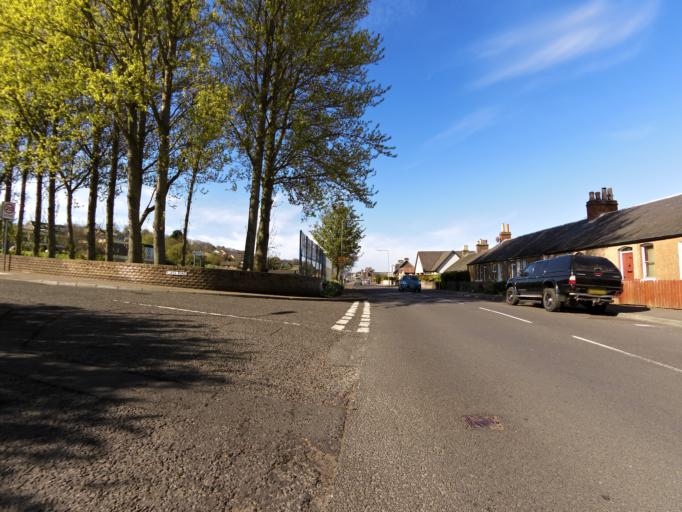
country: GB
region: Scotland
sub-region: Fife
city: Newport-On-Tay
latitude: 56.4307
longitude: -2.9652
